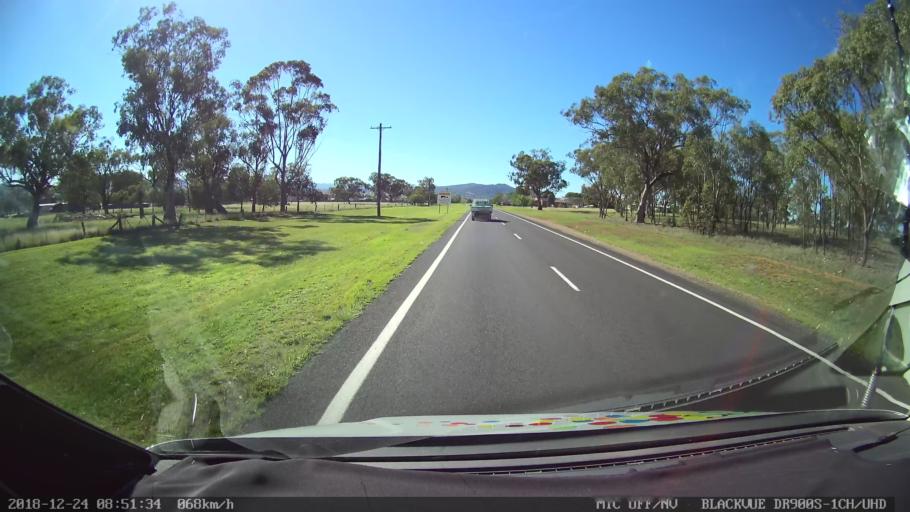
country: AU
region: New South Wales
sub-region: Liverpool Plains
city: Quirindi
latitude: -31.4858
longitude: 150.6750
